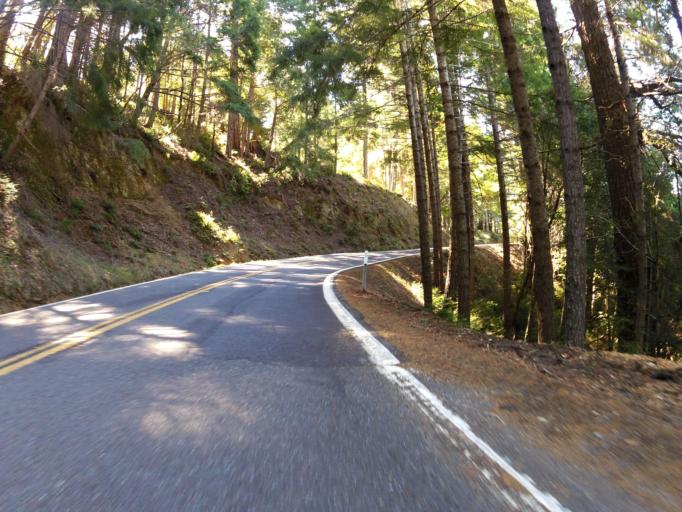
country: US
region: California
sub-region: Humboldt County
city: Redway
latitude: 39.8278
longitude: -123.7779
